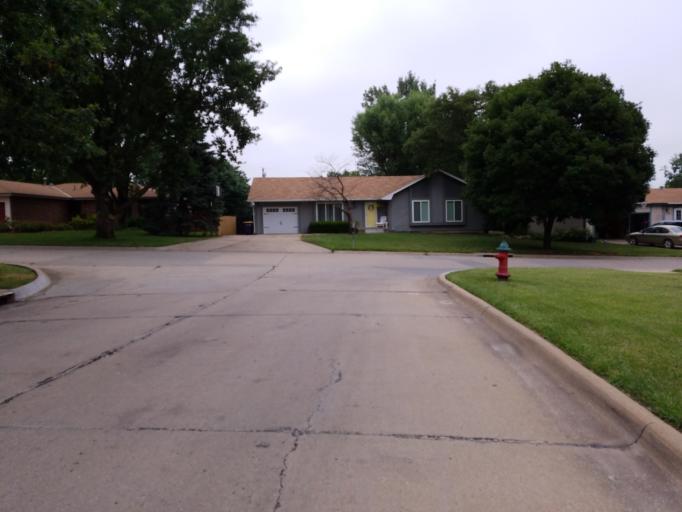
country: US
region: Kansas
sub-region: Riley County
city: Manhattan
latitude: 39.2070
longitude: -96.6216
